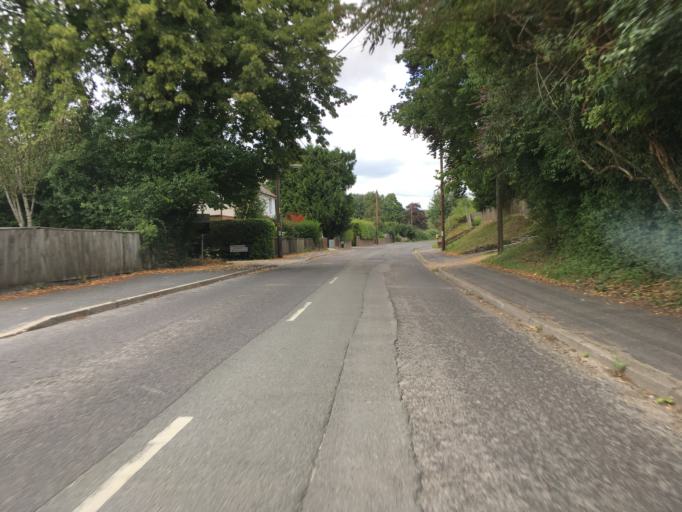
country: GB
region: England
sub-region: Hampshire
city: Kings Worthy
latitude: 51.0935
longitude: -1.3047
